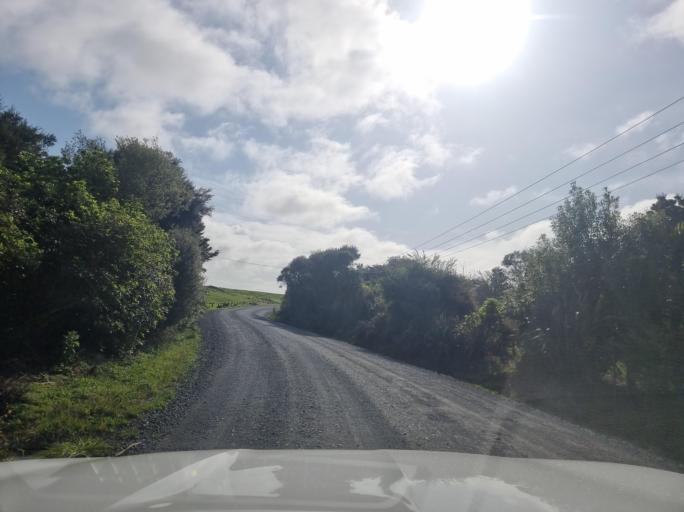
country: NZ
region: Northland
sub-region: Whangarei
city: Ruakaka
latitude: -36.0137
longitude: 174.4670
